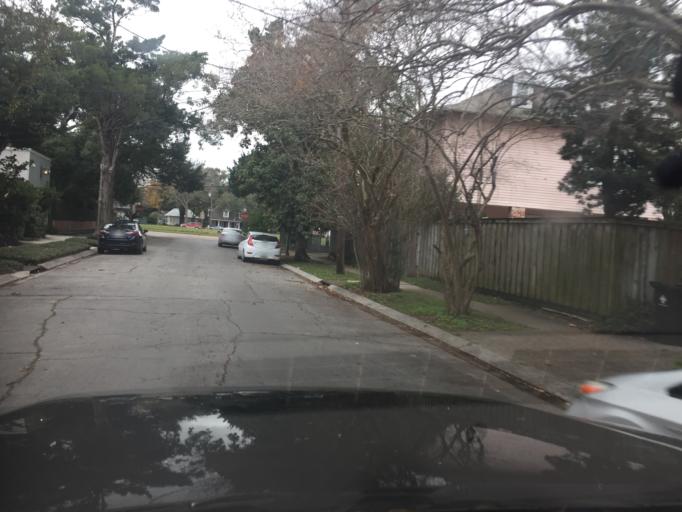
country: US
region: Louisiana
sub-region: Orleans Parish
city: New Orleans
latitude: 29.9783
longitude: -90.0874
